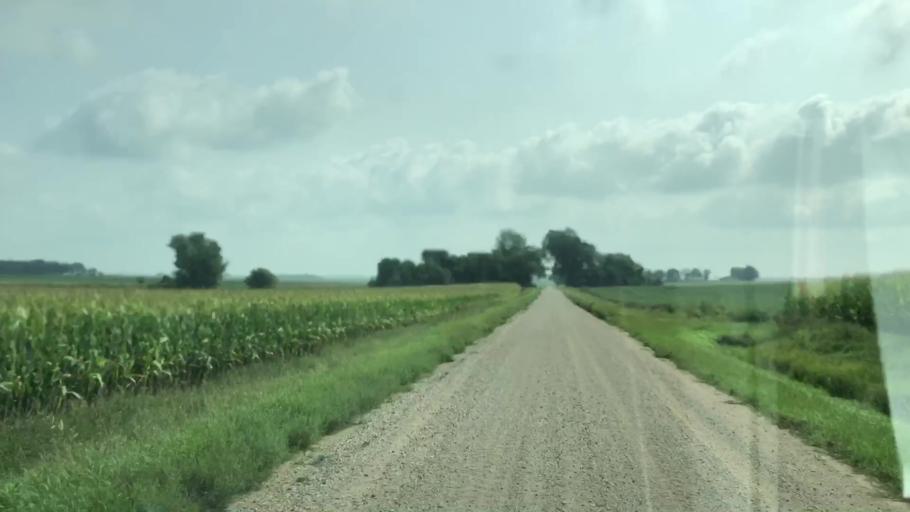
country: US
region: Iowa
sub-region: O'Brien County
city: Sheldon
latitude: 43.2004
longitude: -95.8927
